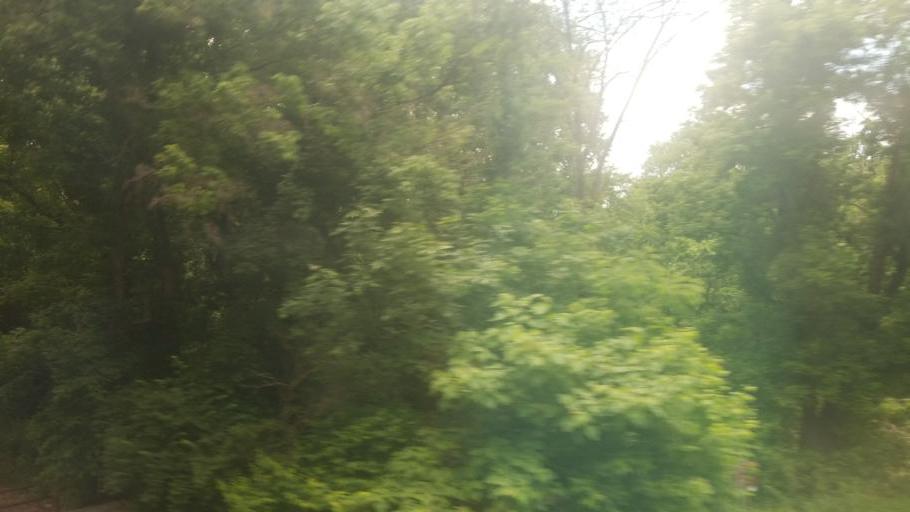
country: US
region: Maryland
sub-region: Frederick County
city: Point of Rocks
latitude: 39.3065
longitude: -77.5577
